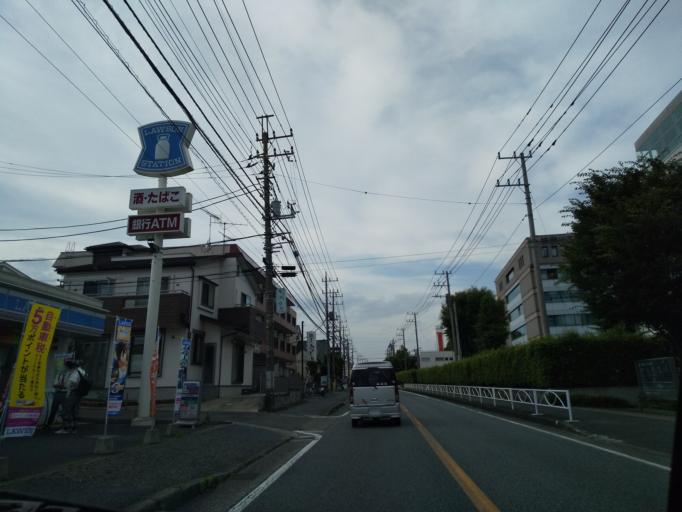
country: JP
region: Kanagawa
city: Zama
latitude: 35.4863
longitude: 139.3406
